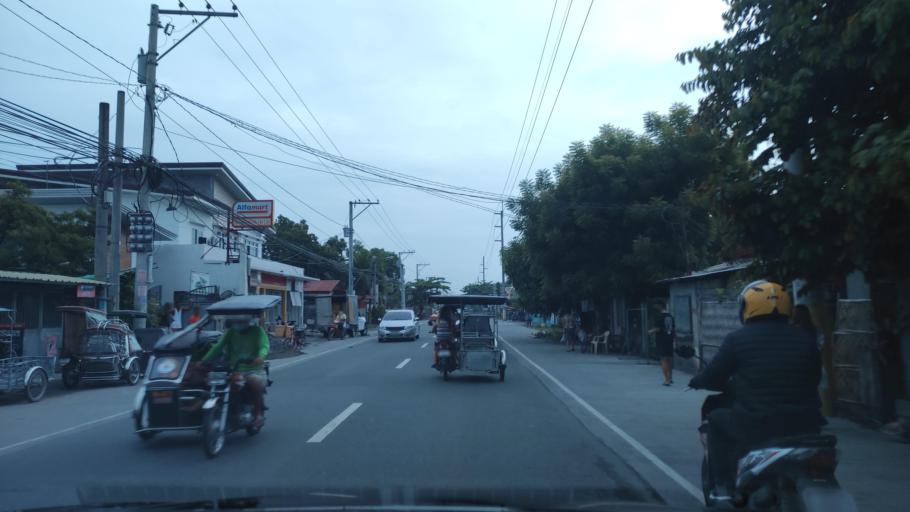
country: PH
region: Central Luzon
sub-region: Province of Pampanga
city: Santa Ana
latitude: 15.1064
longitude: 120.7713
